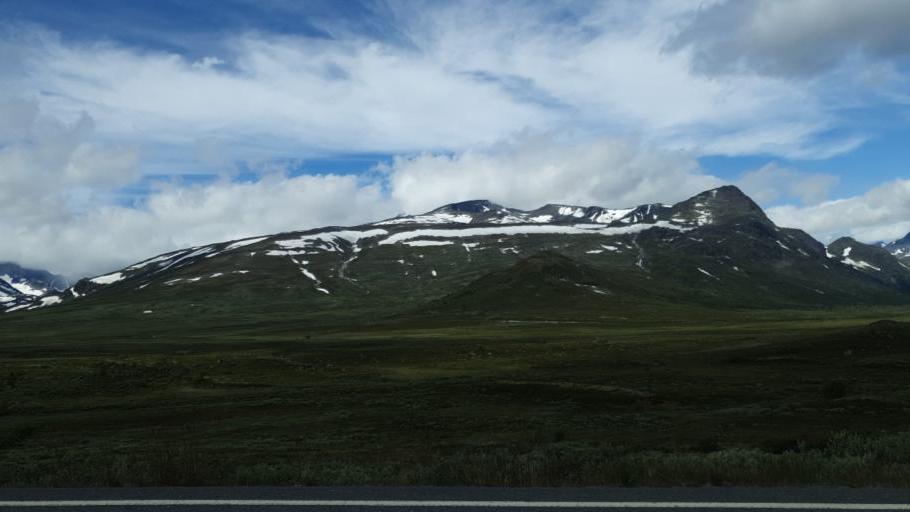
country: NO
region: Oppland
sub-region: Vang
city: Vang
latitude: 61.4535
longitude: 8.8060
